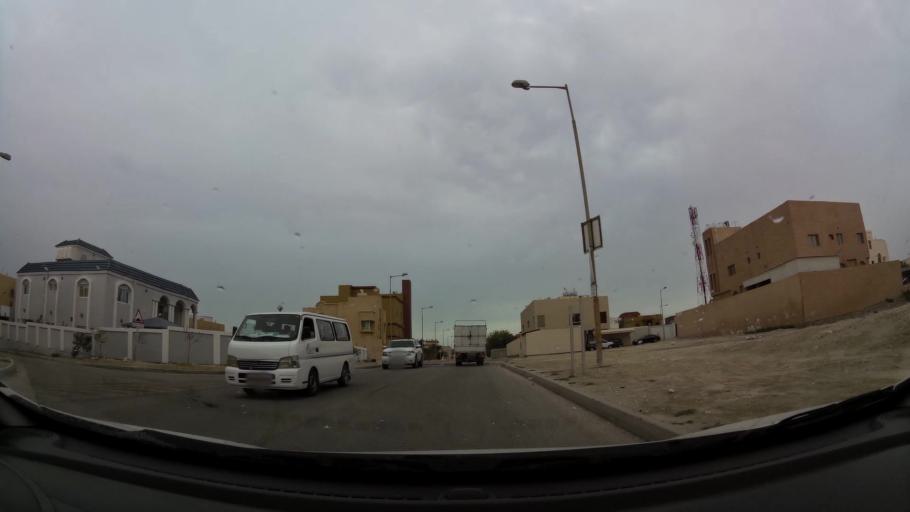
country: BH
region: Central Governorate
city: Madinat Hamad
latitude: 26.1056
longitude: 50.5018
